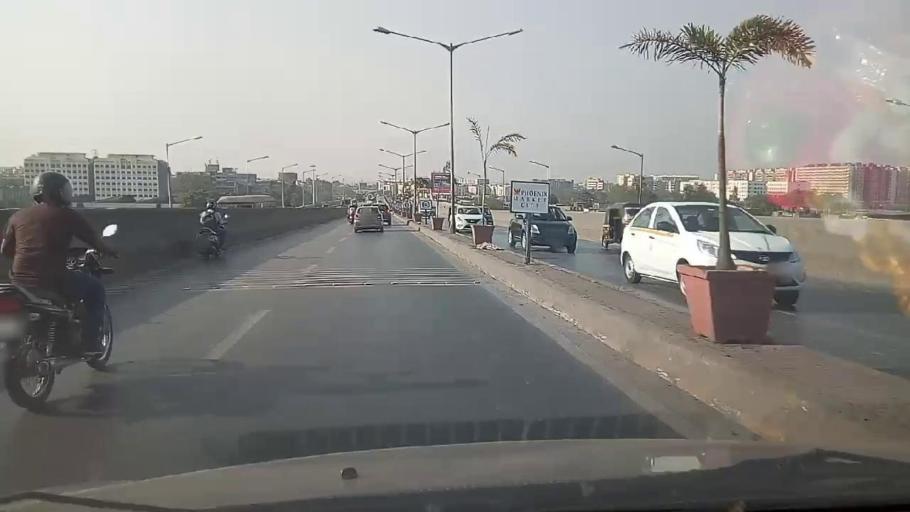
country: IN
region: Maharashtra
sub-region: Mumbai Suburban
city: Mumbai
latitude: 19.0682
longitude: 72.8879
